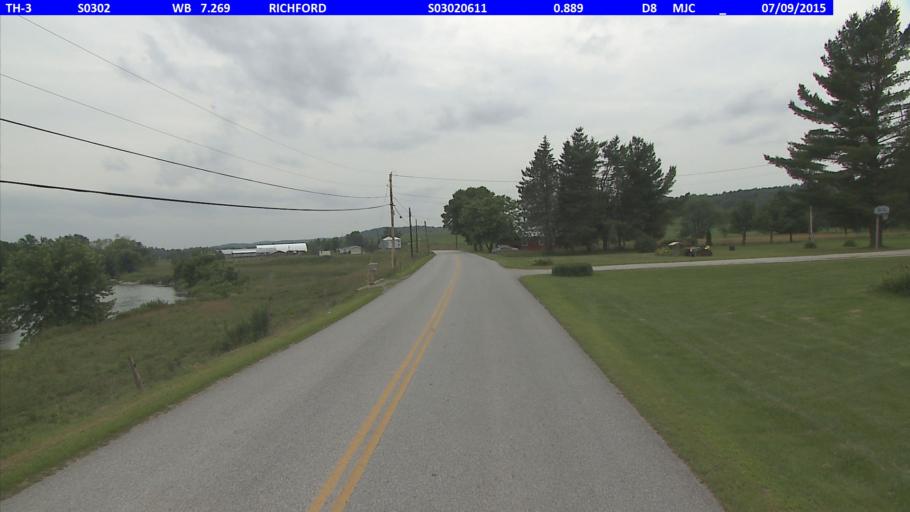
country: US
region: Vermont
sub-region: Franklin County
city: Richford
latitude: 44.9979
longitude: -72.6820
